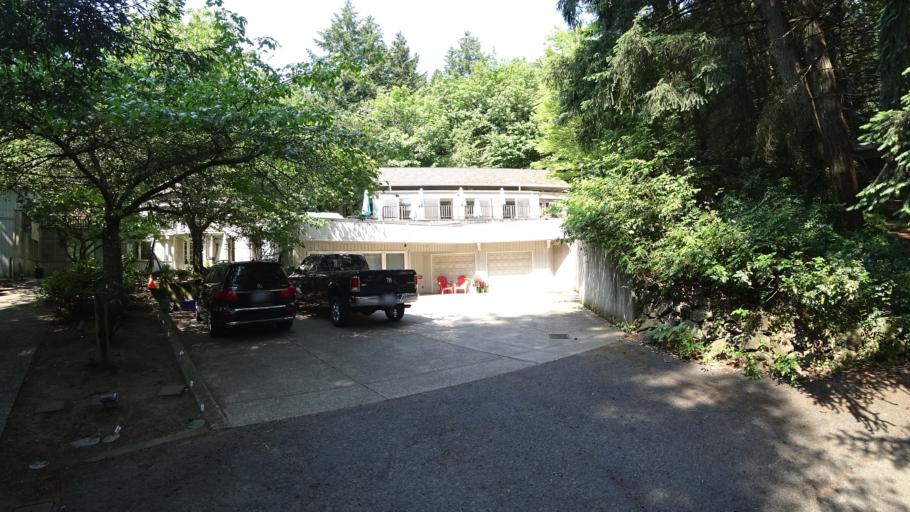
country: US
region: Oregon
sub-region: Clackamas County
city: Happy Valley
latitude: 45.4443
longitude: -122.5557
